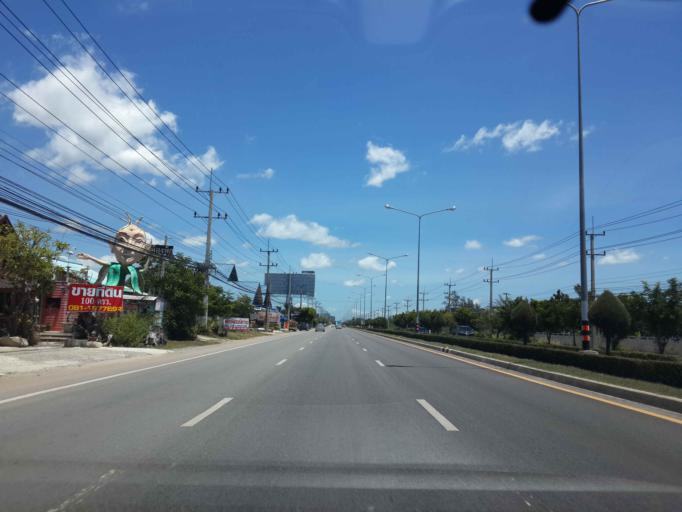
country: TH
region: Phetchaburi
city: Cha-am
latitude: 12.6872
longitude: 99.9528
